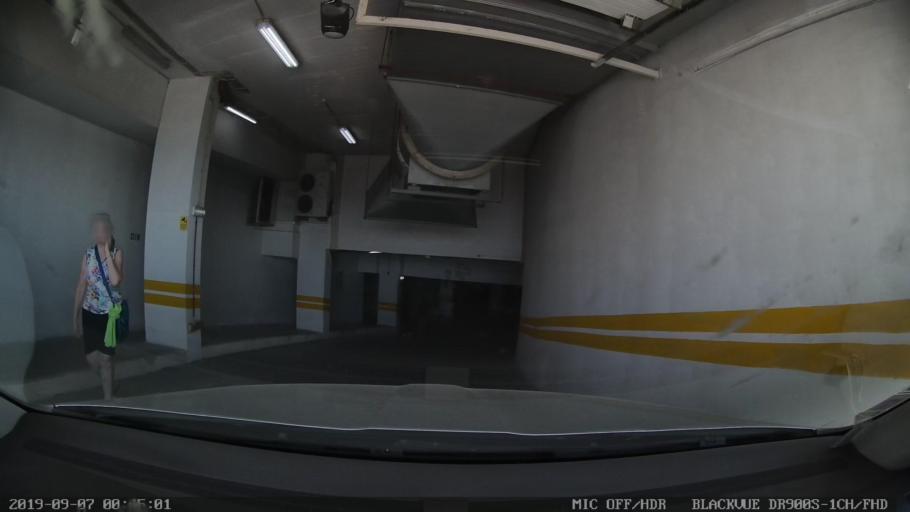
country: PT
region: Setubal
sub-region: Sesimbra
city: Sesimbra
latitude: 38.4426
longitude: -9.0962
